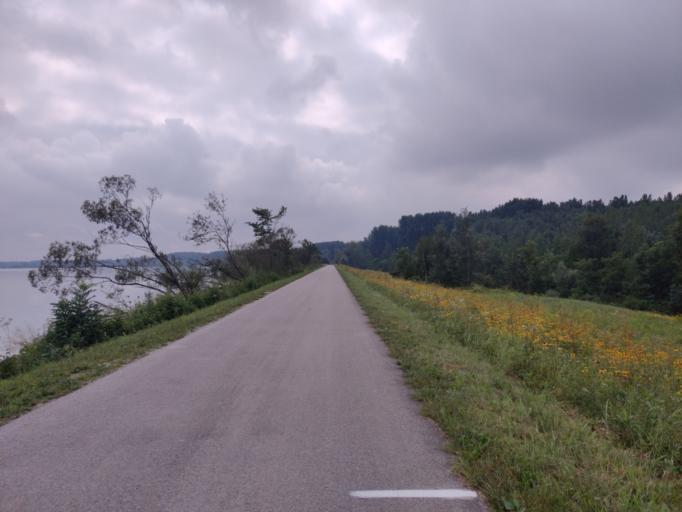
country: AT
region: Lower Austria
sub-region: Politischer Bezirk Sankt Polten
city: Traismauer
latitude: 48.3749
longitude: 15.7335
